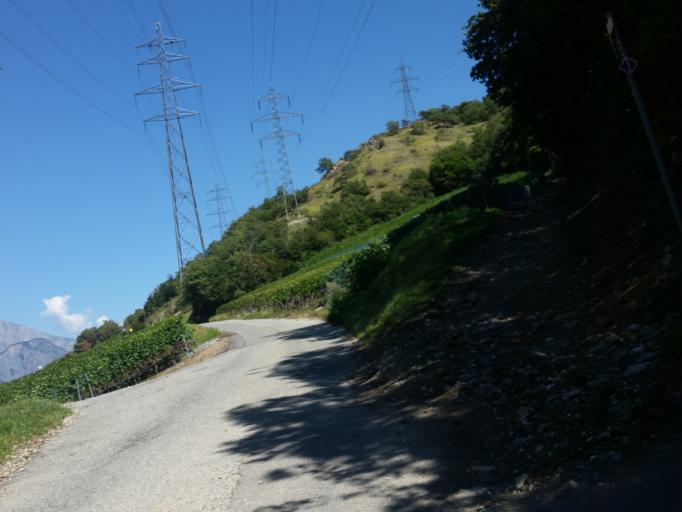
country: CH
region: Valais
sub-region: Martigny District
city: Charrat-les-Chenes
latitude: 46.1254
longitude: 7.1465
